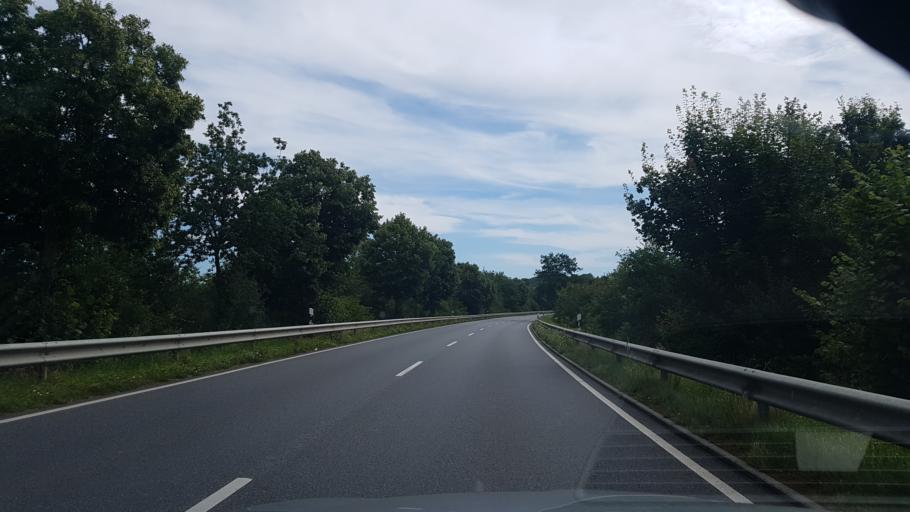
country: DE
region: Schleswig-Holstein
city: Reesdorf
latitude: 54.1887
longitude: 10.0411
